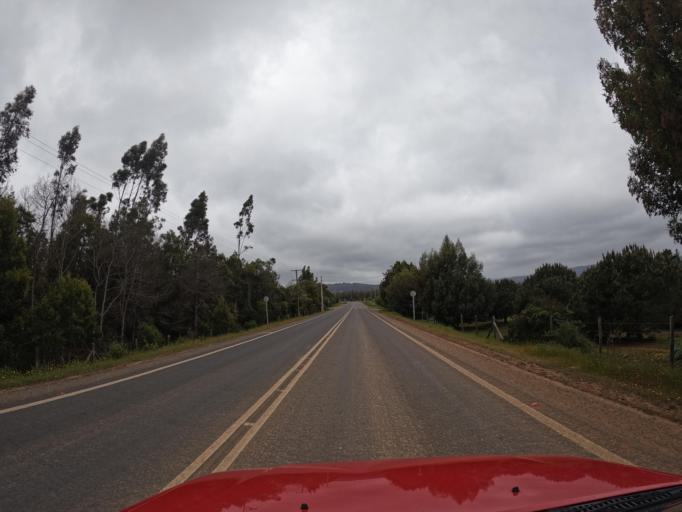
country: CL
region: O'Higgins
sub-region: Provincia de Colchagua
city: Santa Cruz
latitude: -34.5087
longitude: -72.0043
